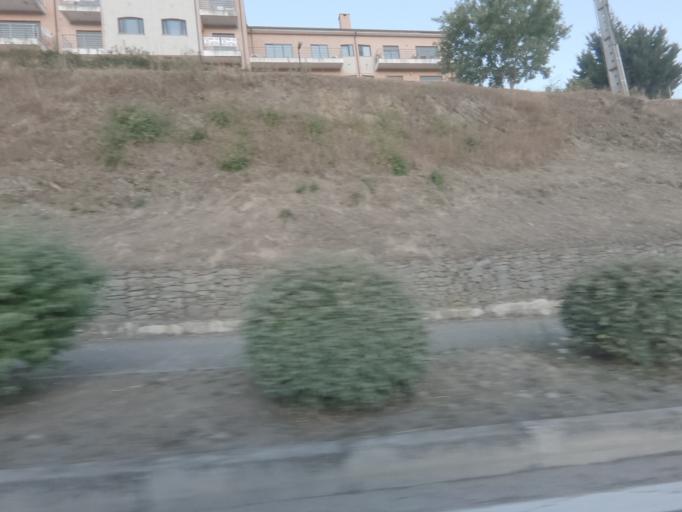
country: PT
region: Vila Real
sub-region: Peso da Regua
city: Peso da Regua
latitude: 41.1606
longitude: -7.7802
